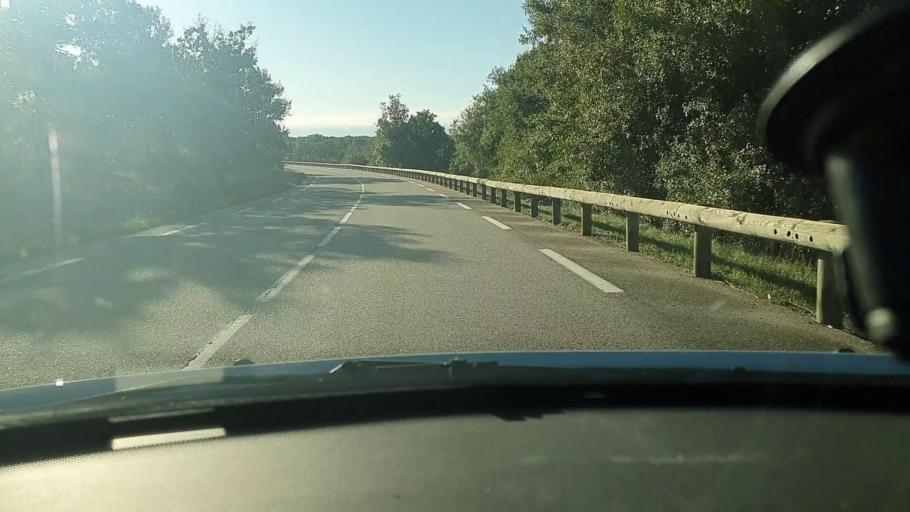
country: FR
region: Languedoc-Roussillon
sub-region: Departement du Gard
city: Barjac
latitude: 44.2179
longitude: 4.3244
